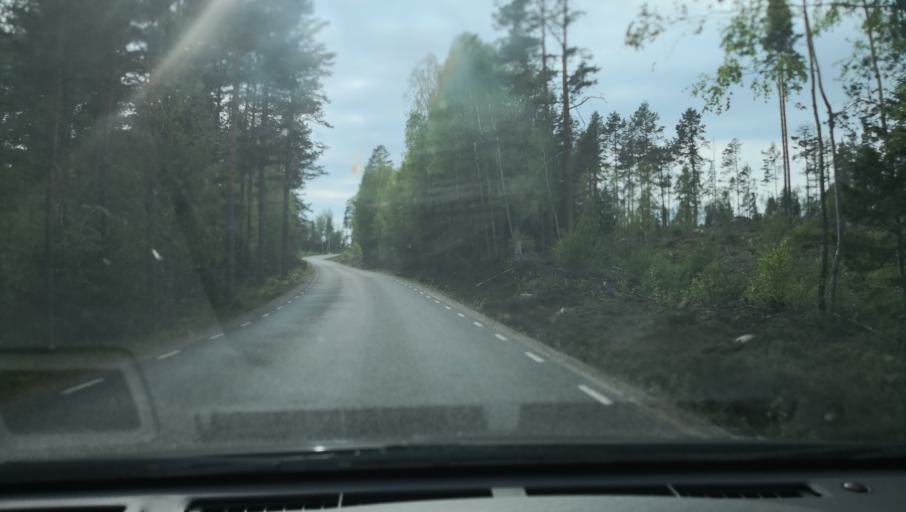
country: SE
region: Vaestmanland
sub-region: Skinnskattebergs Kommun
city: Skinnskatteberg
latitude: 59.8239
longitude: 15.5891
